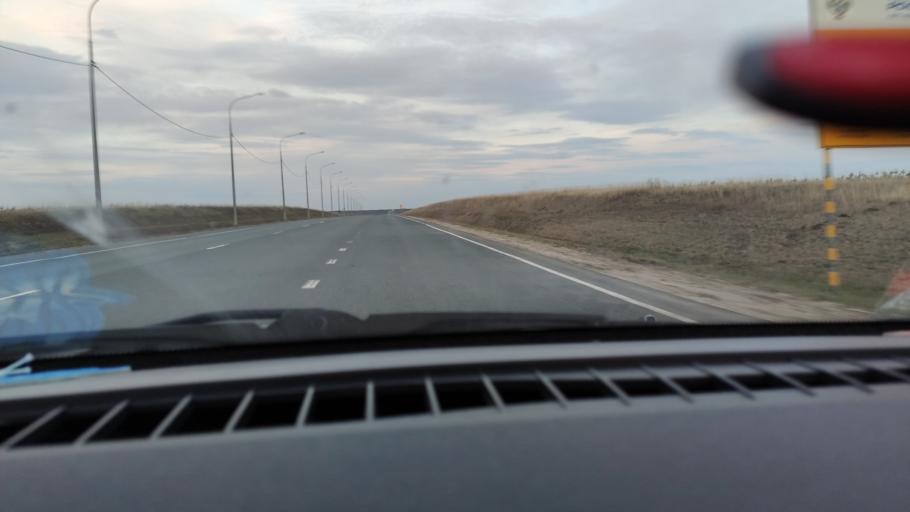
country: RU
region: Saratov
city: Yelshanka
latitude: 51.8310
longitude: 46.4446
